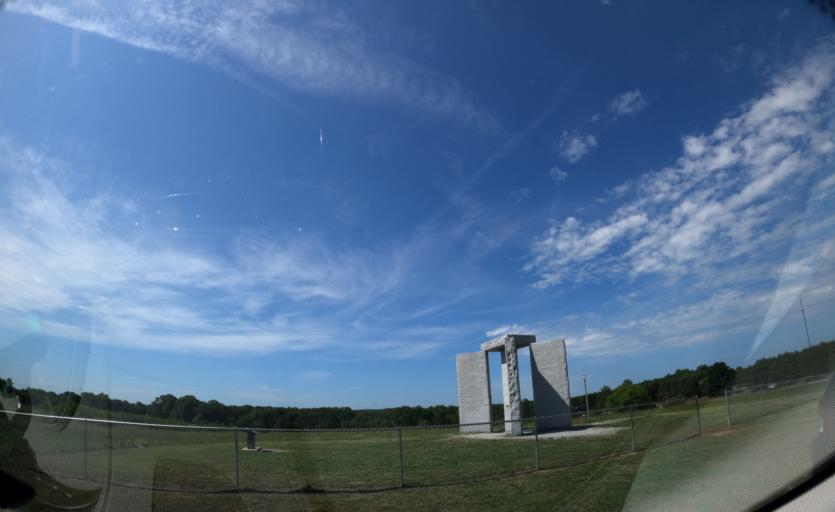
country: US
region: Georgia
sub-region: Elbert County
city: Elberton
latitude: 34.2320
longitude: -82.8945
